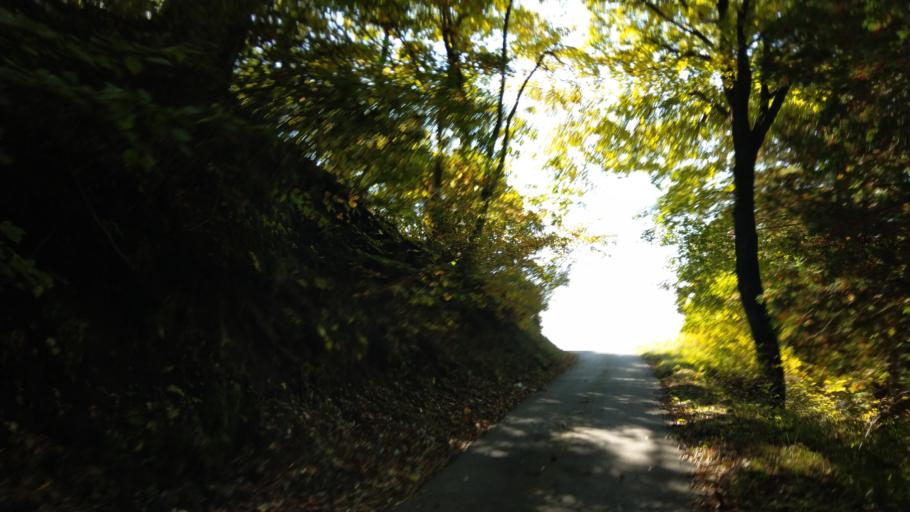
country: JP
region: Nagano
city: Komoro
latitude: 36.3553
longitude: 138.4451
